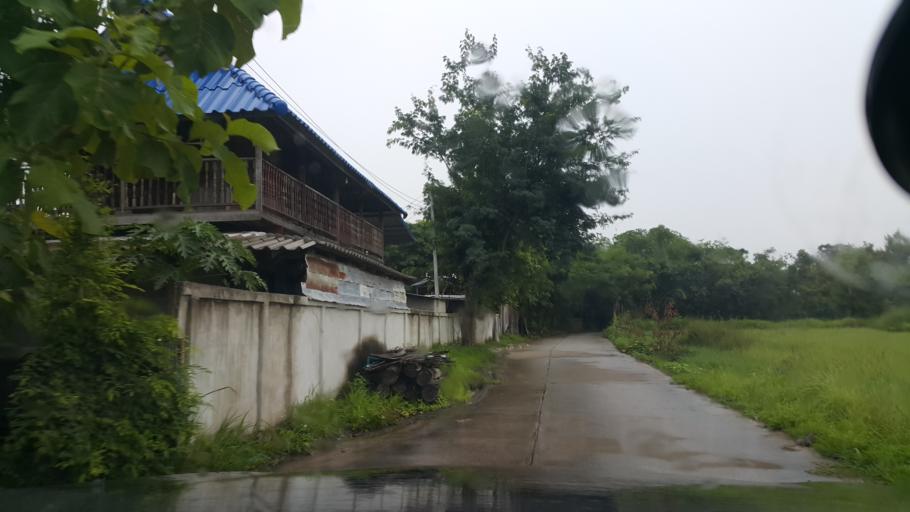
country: TH
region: Lamphun
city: Ban Thi
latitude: 18.6271
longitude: 99.1148
